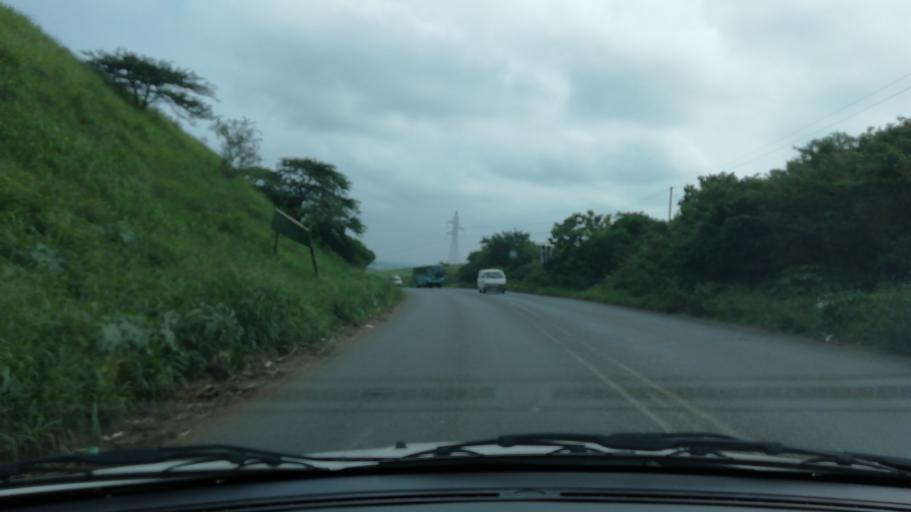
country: ZA
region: KwaZulu-Natal
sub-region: uThungulu District Municipality
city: Empangeni
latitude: -28.7431
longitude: 31.8811
